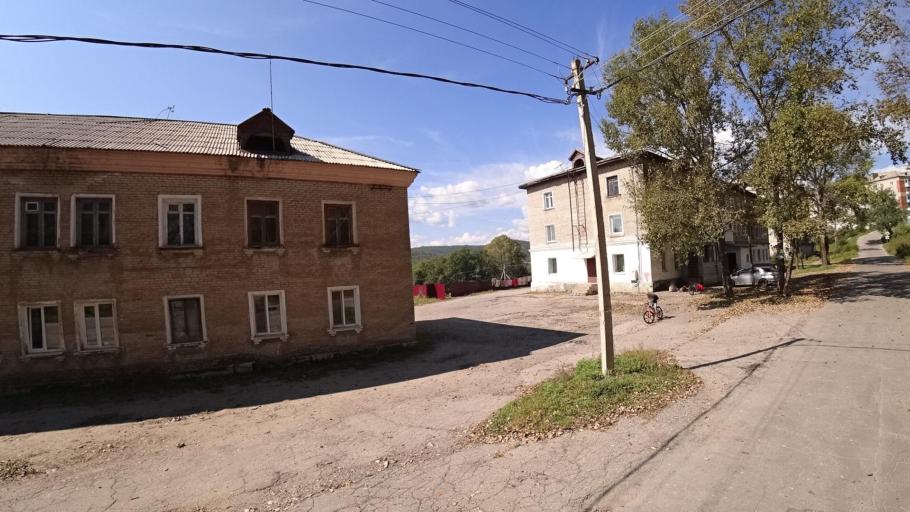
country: RU
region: Jewish Autonomous Oblast
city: Londoko
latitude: 49.0117
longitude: 131.8829
